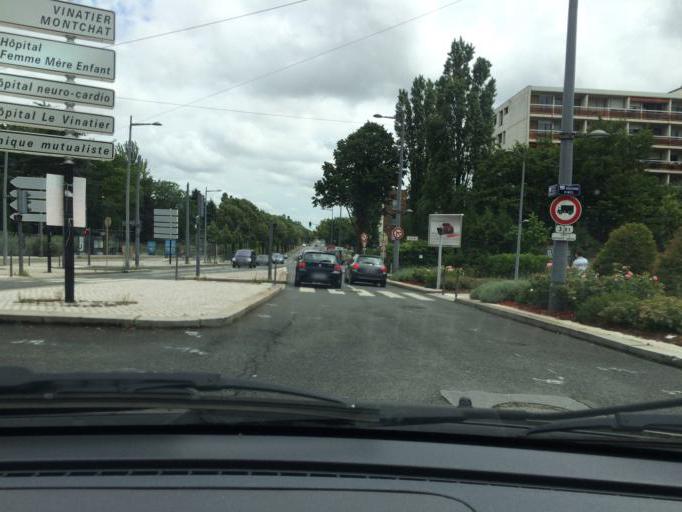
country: FR
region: Rhone-Alpes
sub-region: Departement du Rhone
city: Bron
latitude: 45.7390
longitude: 4.8922
